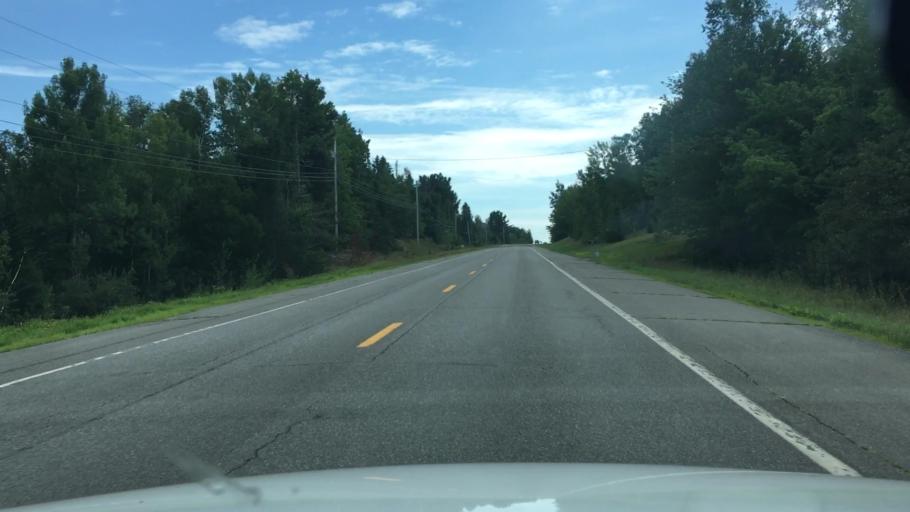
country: CA
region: New Brunswick
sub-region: Charlotte County
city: Saint Andrews
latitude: 45.0523
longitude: -67.1173
